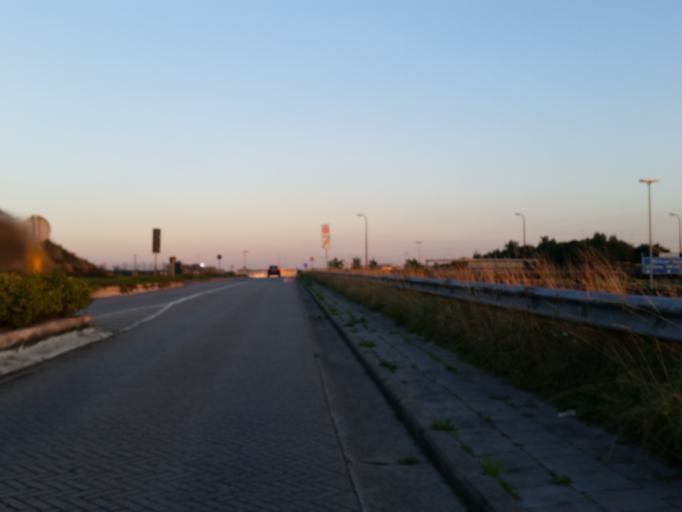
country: BE
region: Flanders
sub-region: Provincie Vlaams-Brabant
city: Diegem
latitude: 50.8985
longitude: 4.4430
